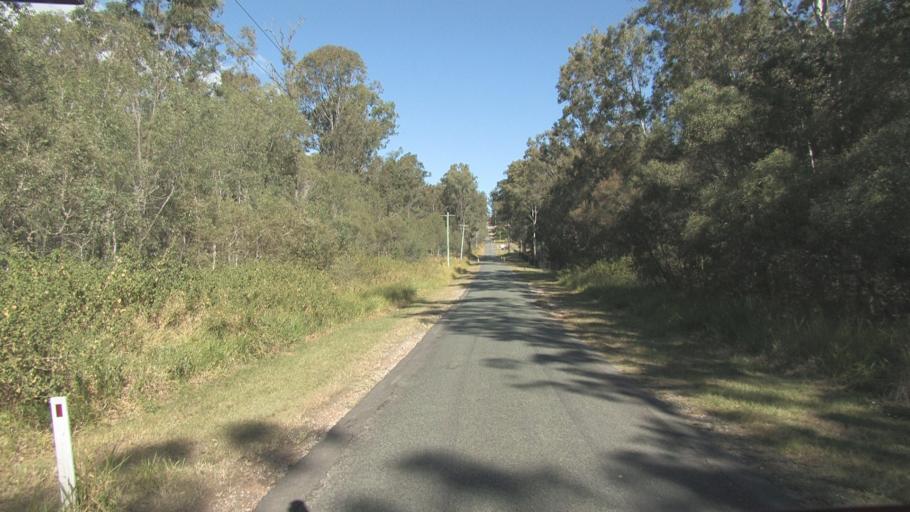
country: AU
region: Queensland
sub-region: Logan
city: Chambers Flat
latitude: -27.8078
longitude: 153.0823
